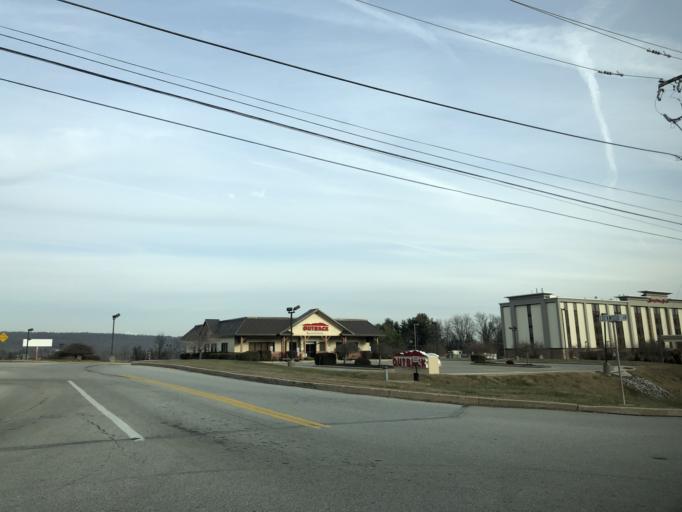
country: US
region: Pennsylvania
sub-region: Chester County
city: Exton
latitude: 40.0337
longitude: -75.5810
